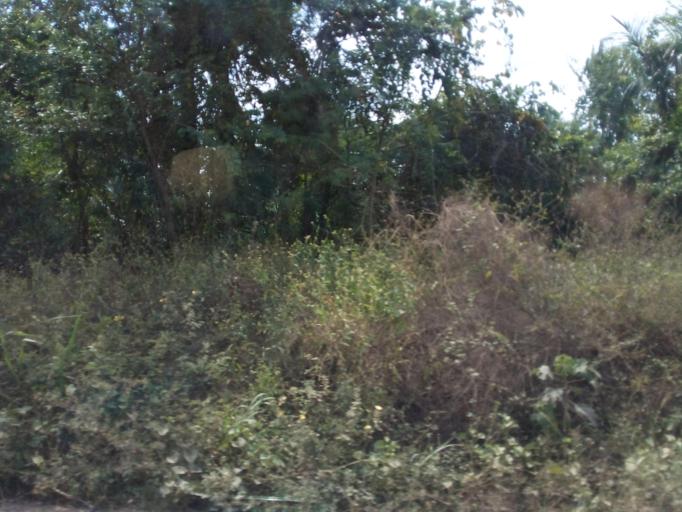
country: BR
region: Maranhao
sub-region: Icatu
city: Icatu
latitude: -2.9248
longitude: -44.3411
